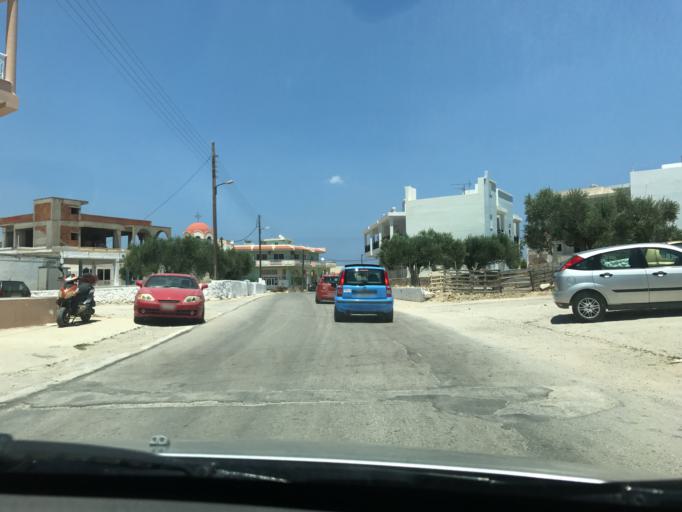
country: GR
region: South Aegean
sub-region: Nomos Dodekanisou
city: Karpathos
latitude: 35.5021
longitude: 27.2105
